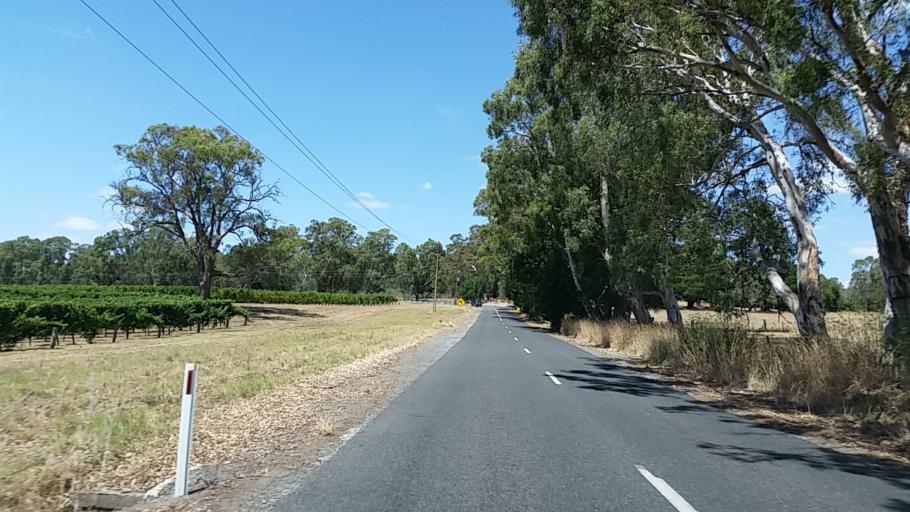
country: AU
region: South Australia
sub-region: Adelaide Hills
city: Woodside
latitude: -34.9674
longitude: 138.8773
